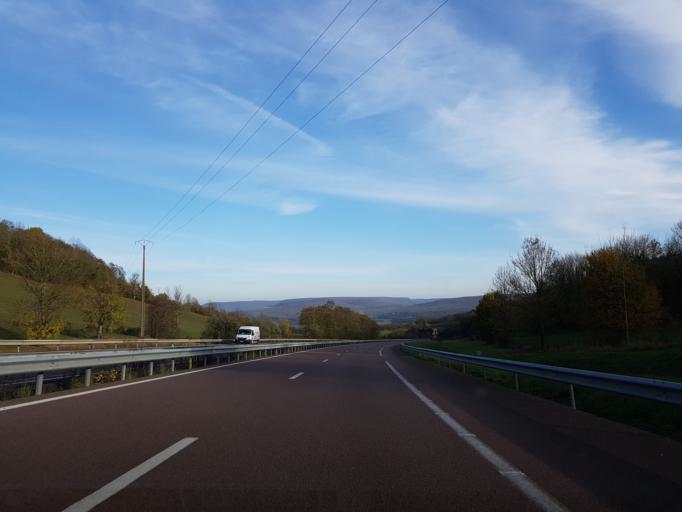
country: FR
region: Bourgogne
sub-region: Departement de la Cote-d'Or
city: Fleurey-sur-Ouche
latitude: 47.3073
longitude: 4.7433
